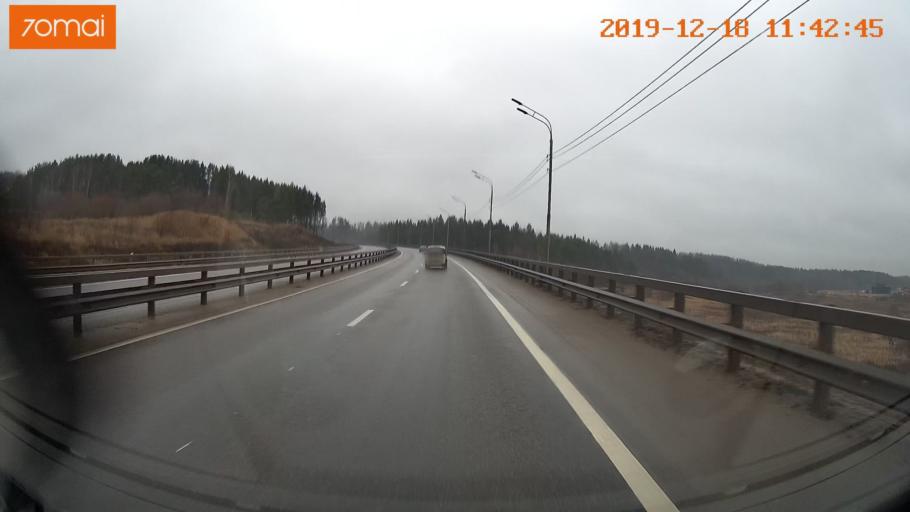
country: RU
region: Moskovskaya
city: Zvenigorod
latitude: 55.7271
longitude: 36.8797
